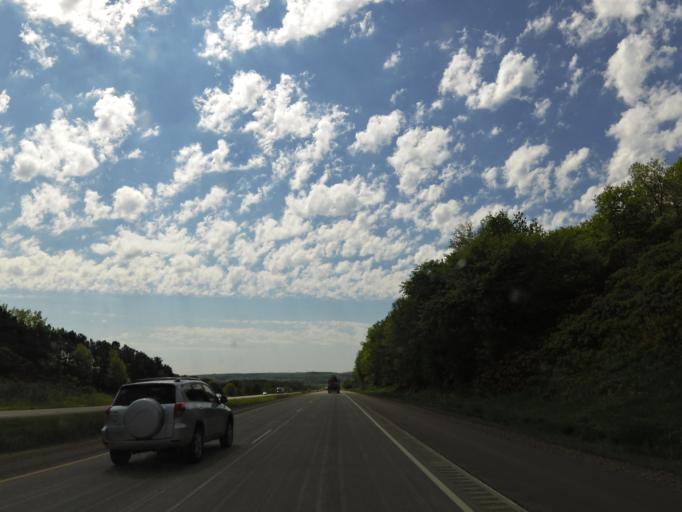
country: US
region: Wisconsin
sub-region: Eau Claire County
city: Eau Claire
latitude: 44.8010
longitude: -91.5550
